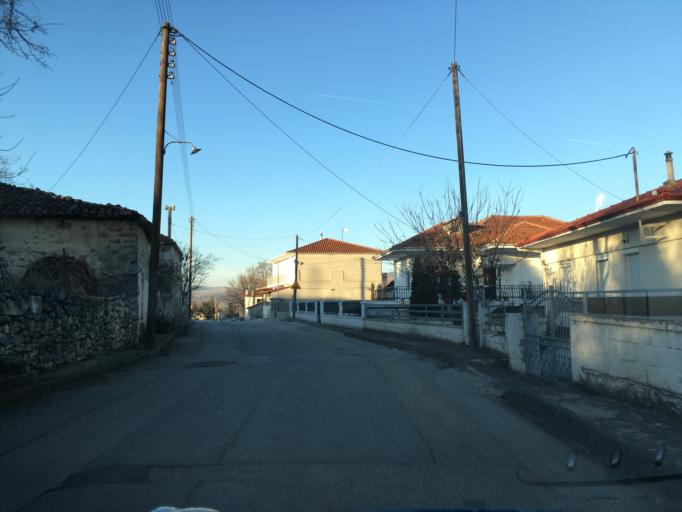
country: GR
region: West Macedonia
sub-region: Nomos Kozanis
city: Kozani
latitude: 40.2849
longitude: 21.7331
